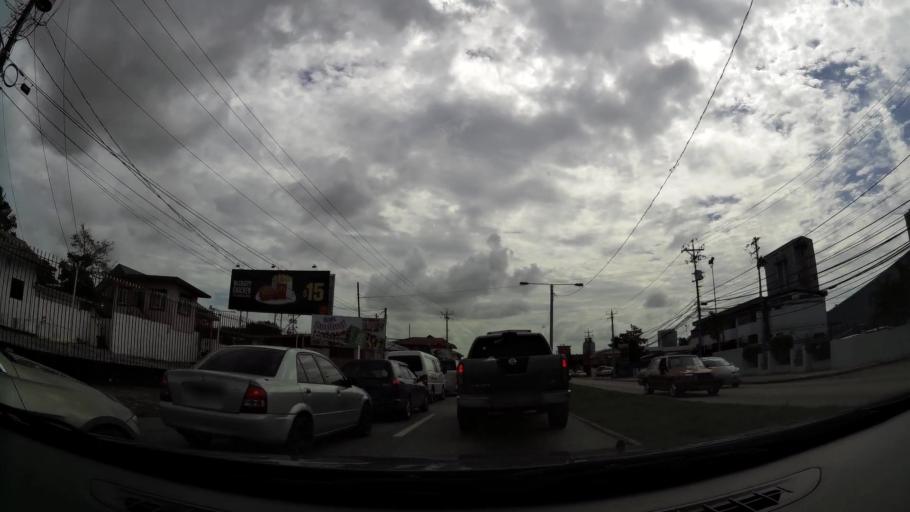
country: TT
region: City of Port of Spain
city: Port-of-Spain
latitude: 10.6597
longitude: -61.5248
